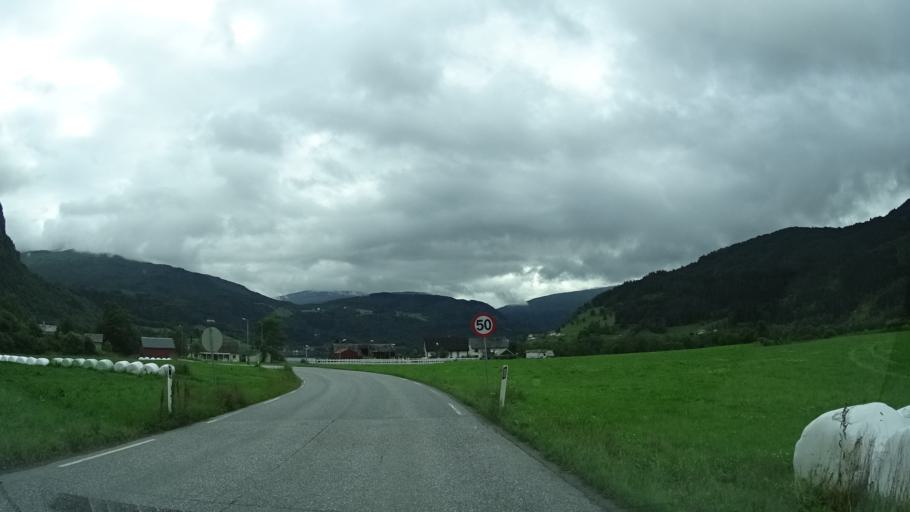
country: NO
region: Hordaland
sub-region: Granvin
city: Granvin
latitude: 60.5720
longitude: 6.6951
